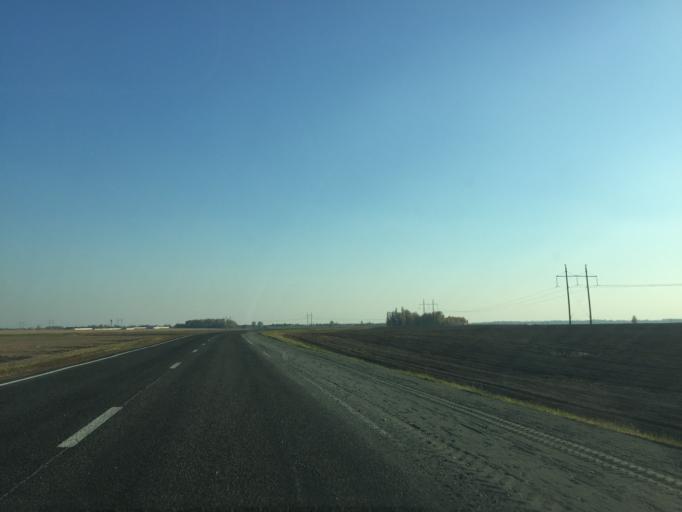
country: BY
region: Gomel
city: Dobrush
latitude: 52.3251
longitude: 31.2441
